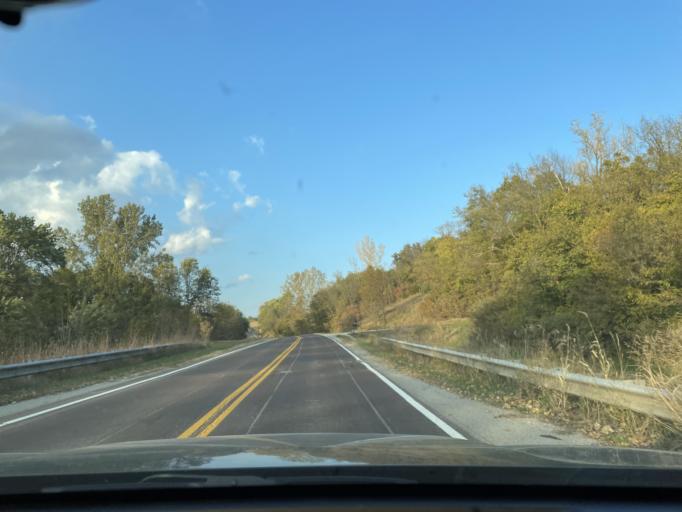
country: US
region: Missouri
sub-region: Andrew County
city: Savannah
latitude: 39.9070
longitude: -94.8796
